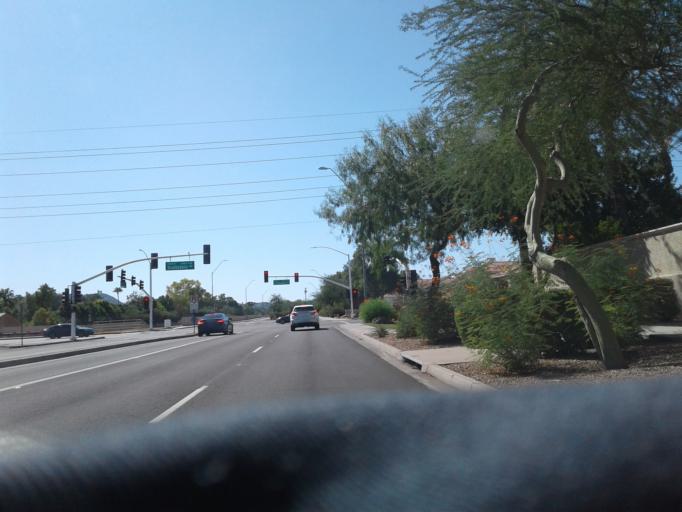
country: US
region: Arizona
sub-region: Maricopa County
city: Paradise Valley
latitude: 33.5751
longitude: -111.9252
